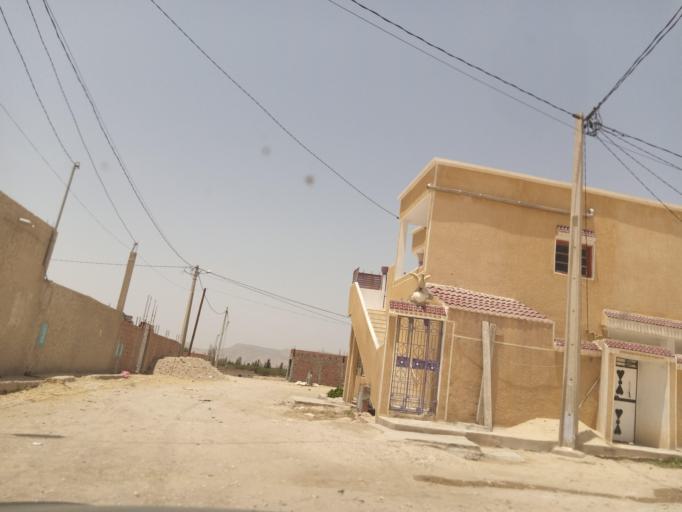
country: TN
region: Al Qasrayn
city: Kasserine
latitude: 35.2123
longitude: 8.8918
